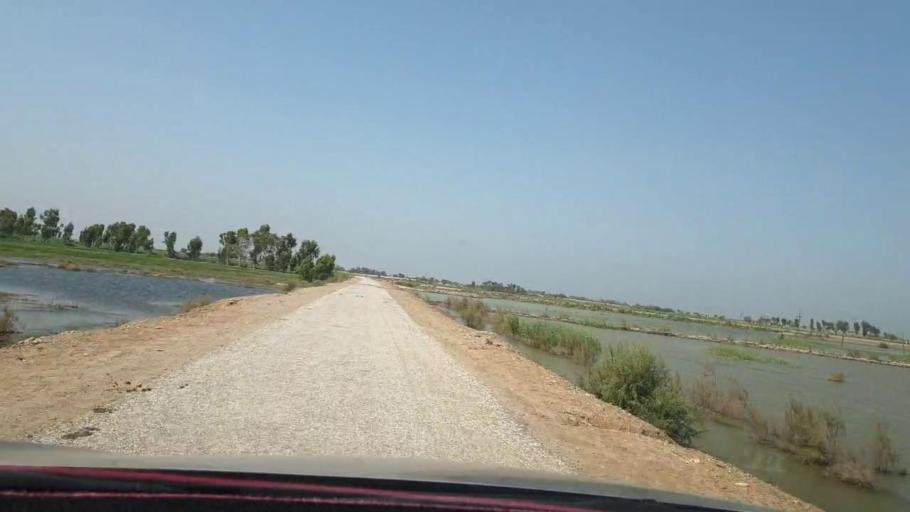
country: PK
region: Sindh
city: Warah
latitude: 27.5445
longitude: 67.7436
